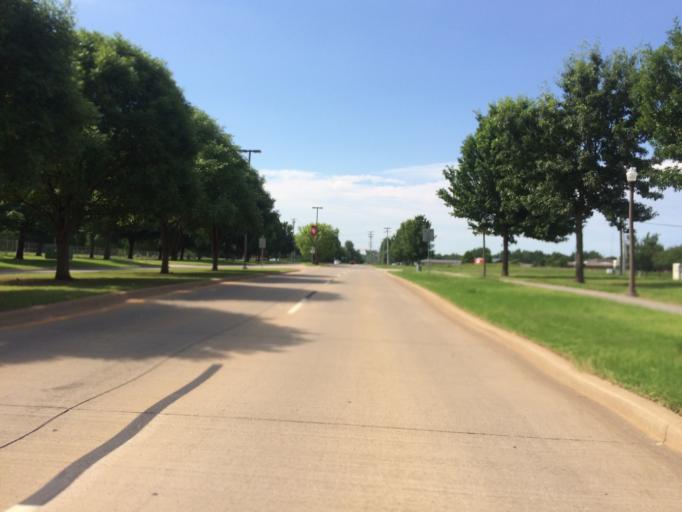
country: US
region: Oklahoma
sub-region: Cleveland County
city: Norman
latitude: 35.1842
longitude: -97.4502
